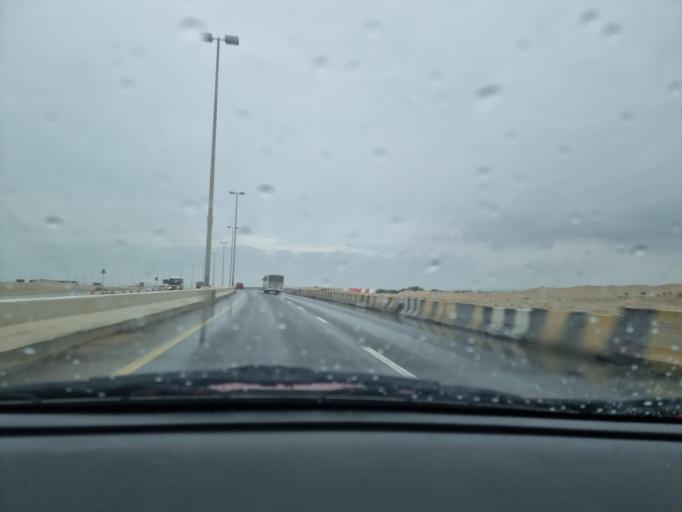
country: AE
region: Abu Dhabi
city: Abu Dhabi
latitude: 24.4736
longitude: 54.6687
